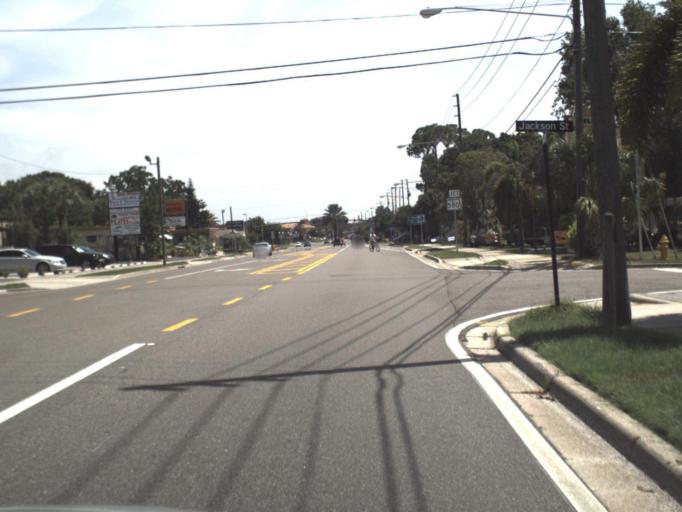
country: US
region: Florida
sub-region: Pinellas County
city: Dunedin
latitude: 28.0181
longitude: -82.7899
